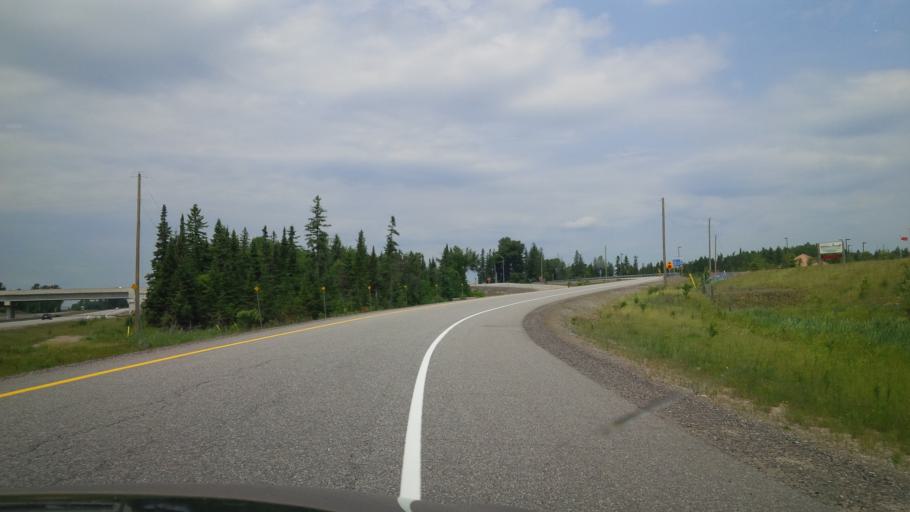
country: CA
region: Ontario
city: Huntsville
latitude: 45.5097
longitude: -79.3039
